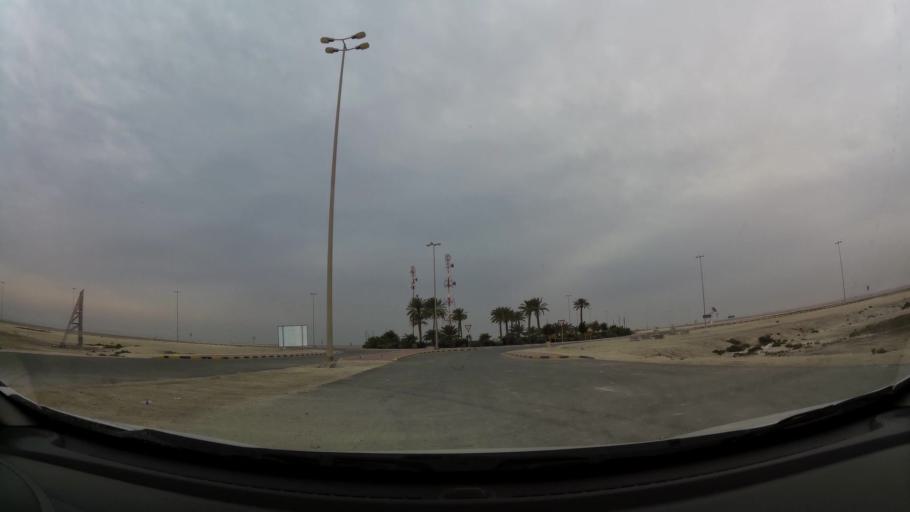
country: BH
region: Central Governorate
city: Dar Kulayb
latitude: 25.8453
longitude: 50.5863
